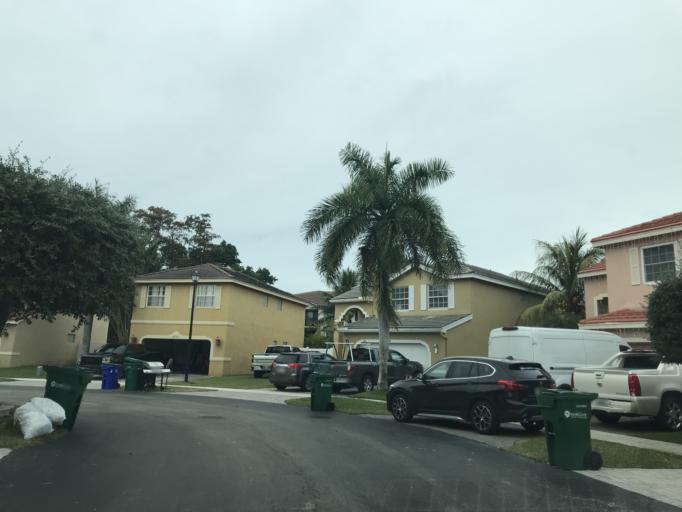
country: US
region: Florida
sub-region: Broward County
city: Margate
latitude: 26.2658
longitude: -80.2030
